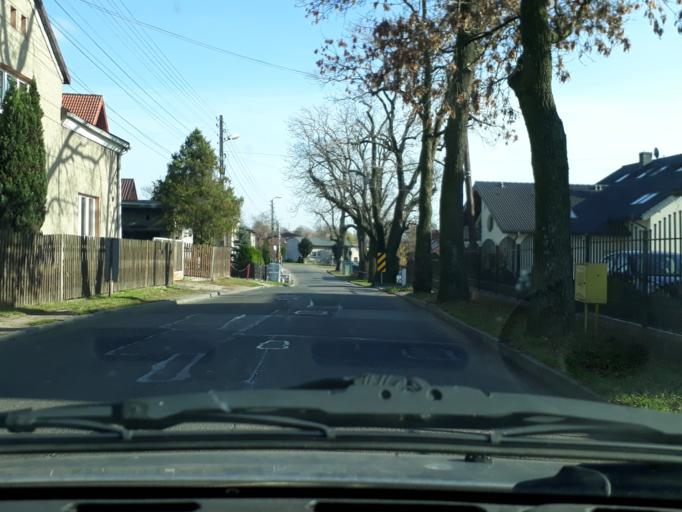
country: PL
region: Silesian Voivodeship
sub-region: Powiat tarnogorski
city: Tarnowskie Gory
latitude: 50.4241
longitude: 18.8587
